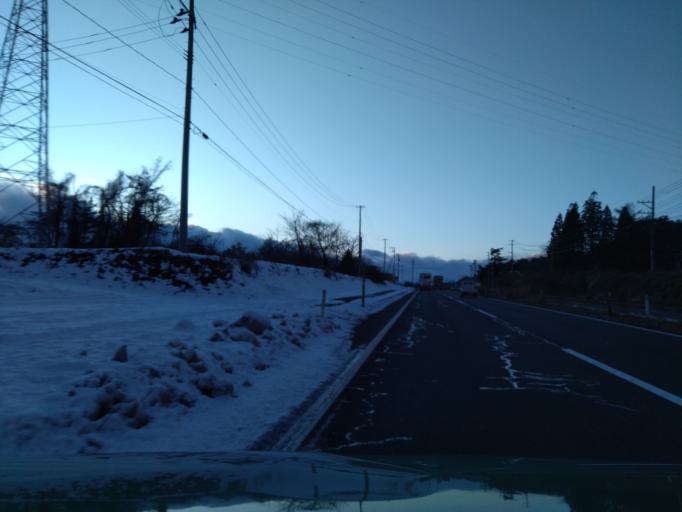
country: JP
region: Iwate
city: Shizukuishi
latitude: 39.7020
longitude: 141.0398
